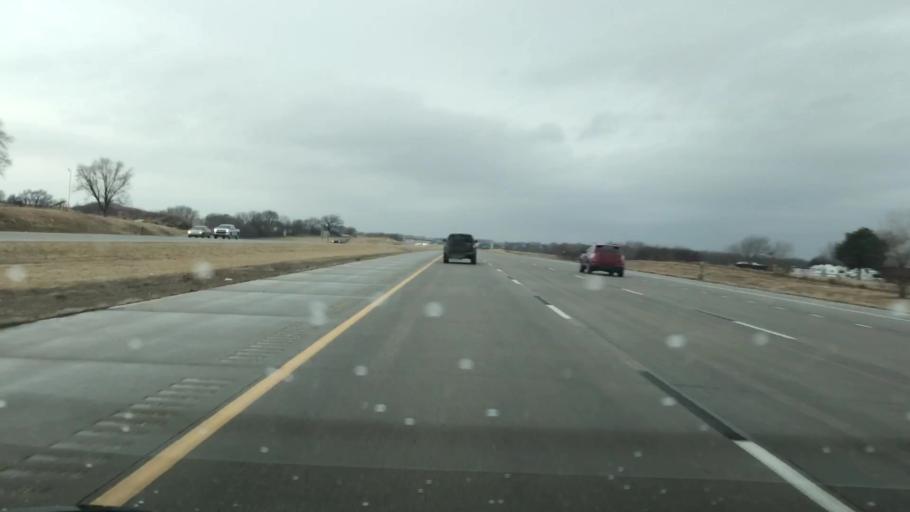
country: US
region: Nebraska
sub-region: Saunders County
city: Ashland
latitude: 40.9684
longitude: -96.3936
